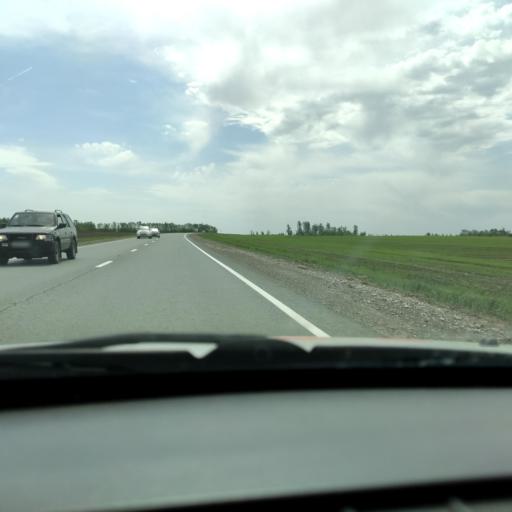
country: RU
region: Samara
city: Novyy Buyan
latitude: 53.6838
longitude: 50.2192
